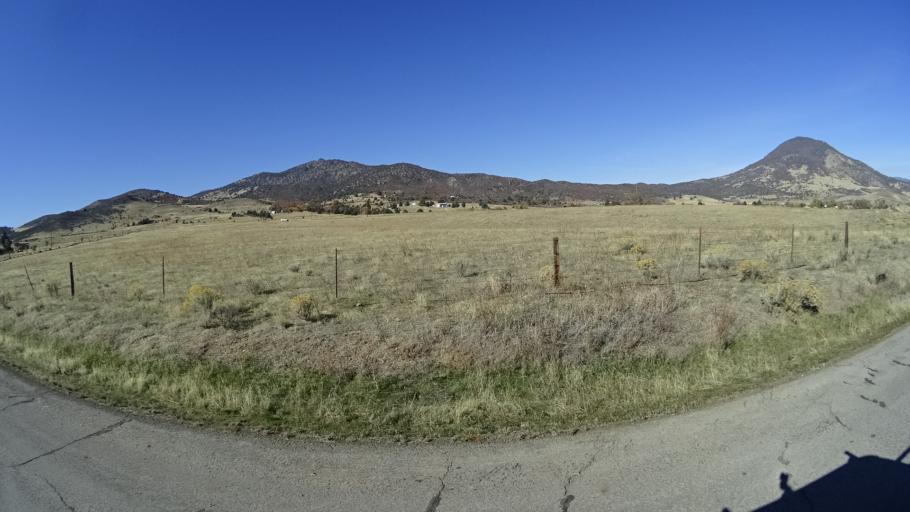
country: US
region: California
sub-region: Siskiyou County
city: Montague
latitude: 41.8051
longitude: -122.4985
